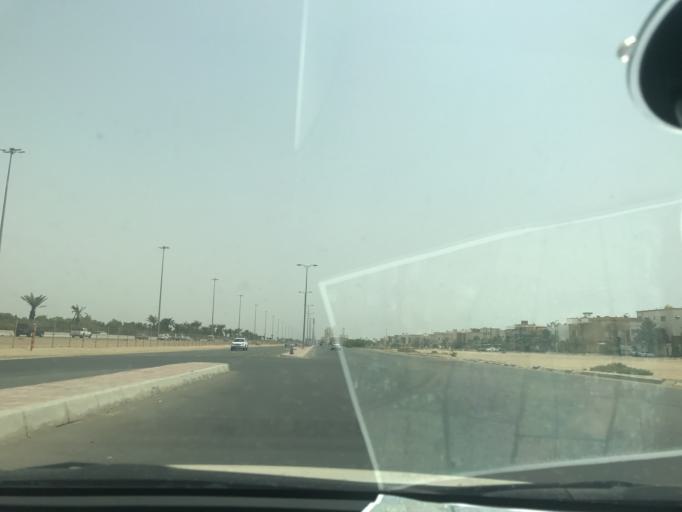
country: SA
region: Makkah
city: Jeddah
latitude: 21.6935
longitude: 39.1193
